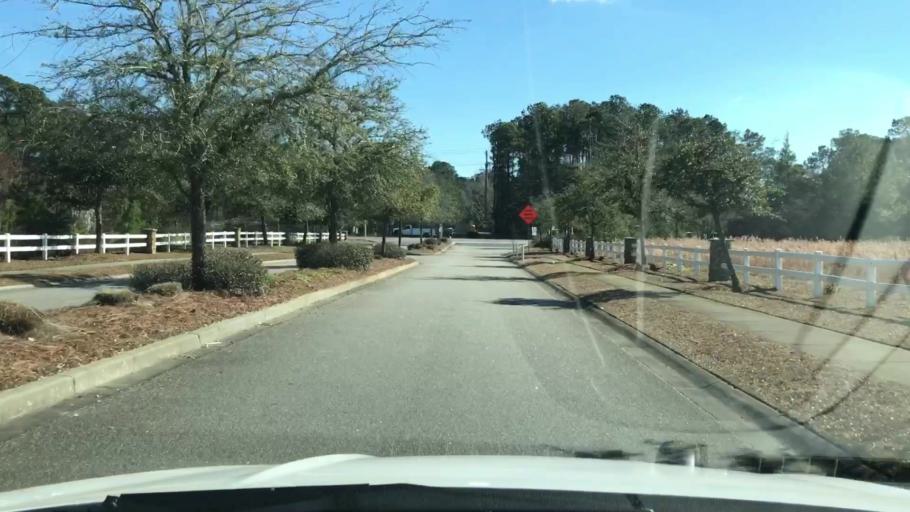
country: US
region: South Carolina
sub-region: Horry County
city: Garden City
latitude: 33.6409
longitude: -79.0318
